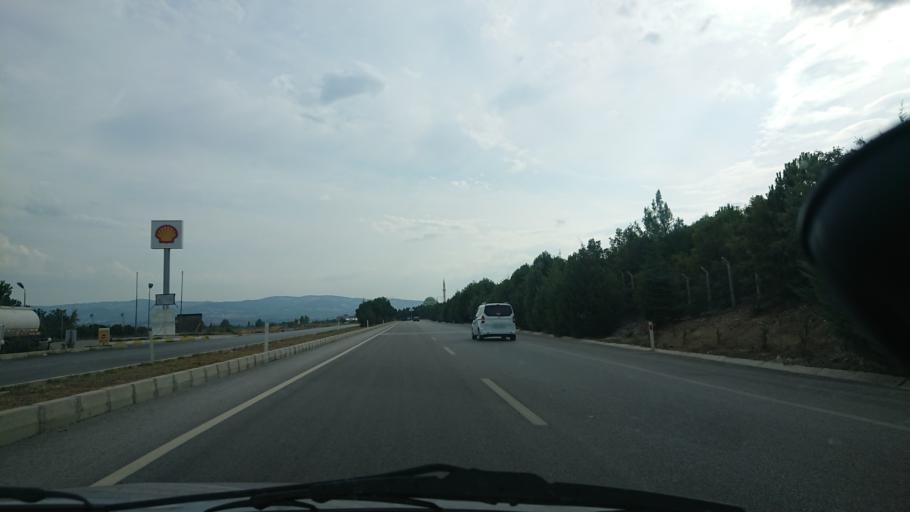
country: TR
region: Kuetahya
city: Gediz
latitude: 39.0090
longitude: 29.4077
